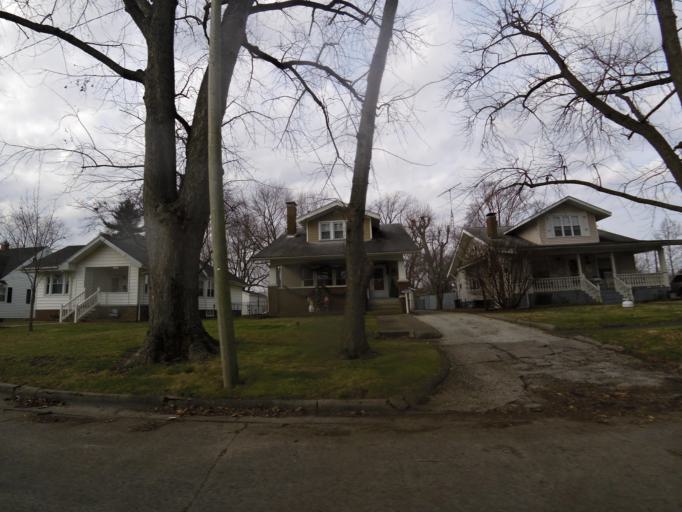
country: US
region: Illinois
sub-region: Christian County
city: Pana
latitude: 39.3774
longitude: -89.0830
